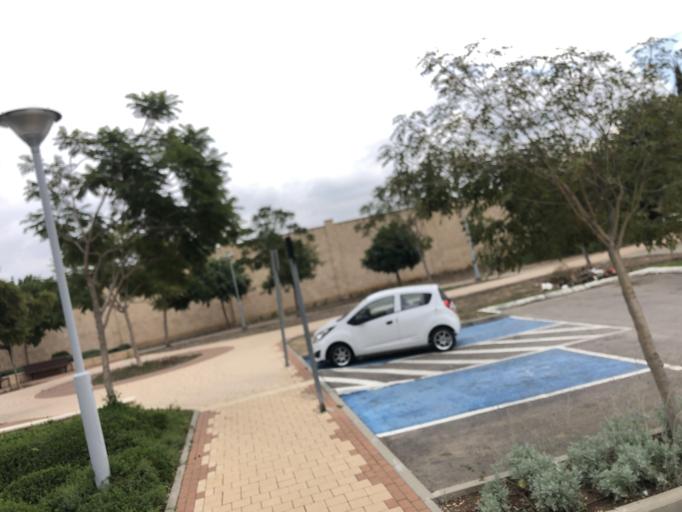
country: IL
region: Northern District
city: `Akko
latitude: 32.9282
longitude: 35.0962
